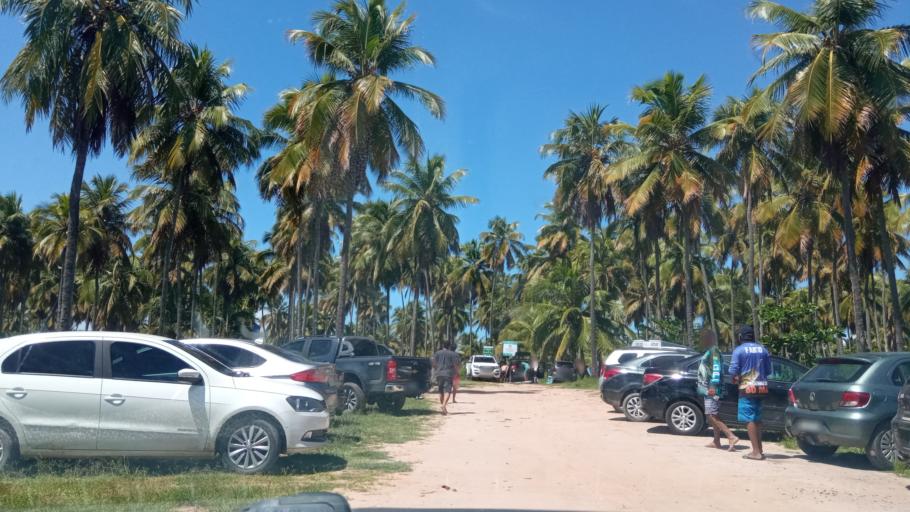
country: BR
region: Pernambuco
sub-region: Cabo De Santo Agostinho
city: Cabo
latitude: -8.2602
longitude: -34.9470
